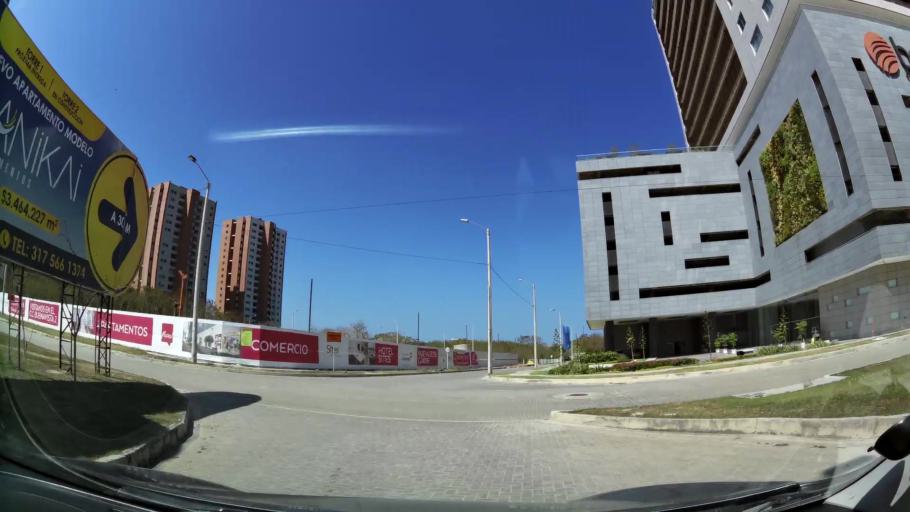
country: CO
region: Atlantico
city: Barranquilla
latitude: 11.0193
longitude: -74.8392
